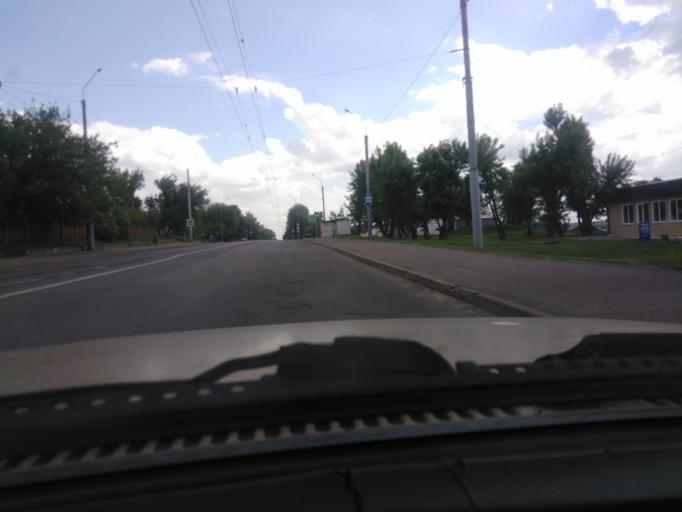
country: BY
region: Mogilev
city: Mahilyow
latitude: 53.9349
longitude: 30.3349
